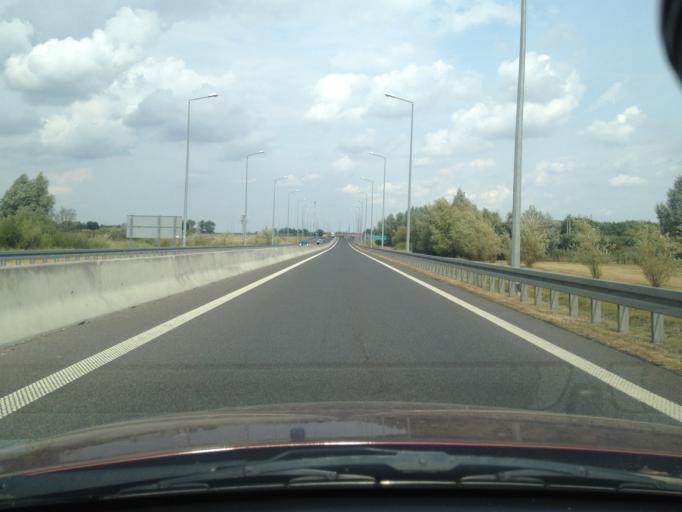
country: PL
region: West Pomeranian Voivodeship
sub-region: Powiat pyrzycki
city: Lipiany
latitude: 52.9457
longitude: 14.9485
